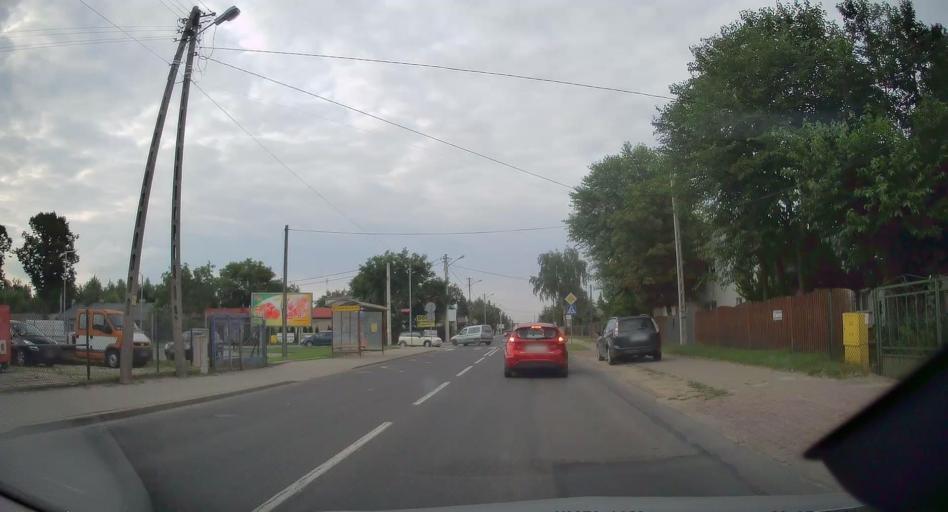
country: PL
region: Lodz Voivodeship
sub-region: Powiat radomszczanski
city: Radomsko
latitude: 51.0848
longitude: 19.4534
